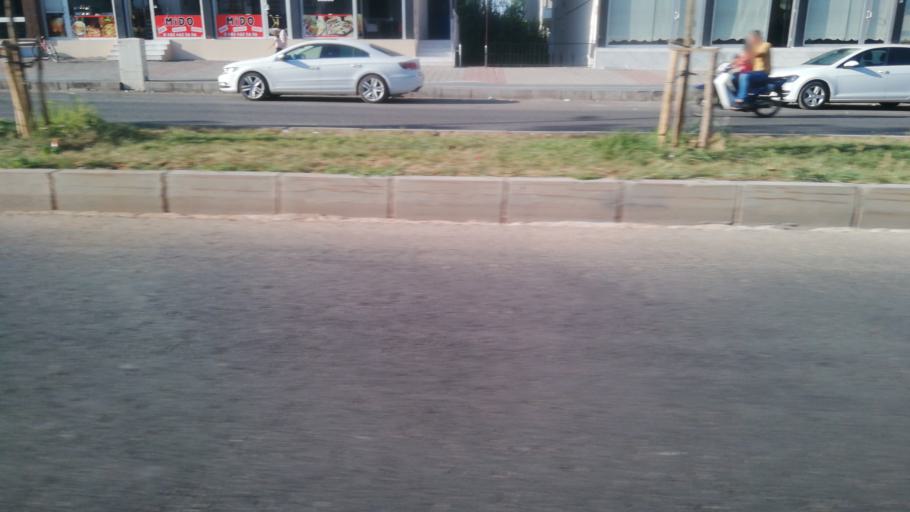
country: TR
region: Mardin
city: Midyat
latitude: 37.4172
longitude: 41.3621
